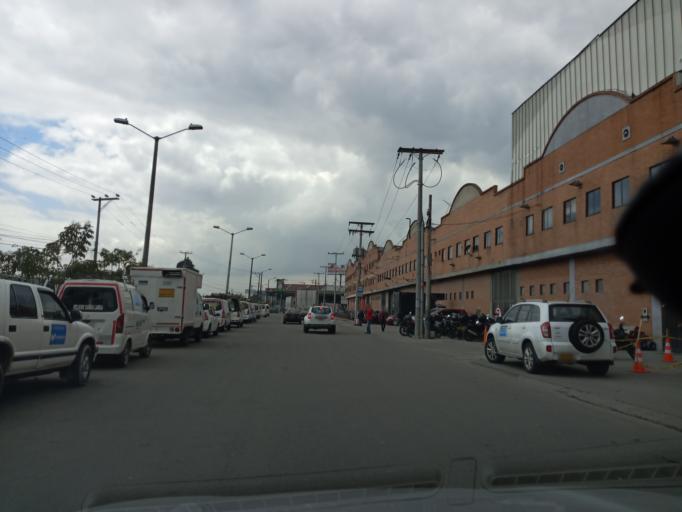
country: CO
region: Bogota D.C.
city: Bogota
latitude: 4.6461
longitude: -74.1234
